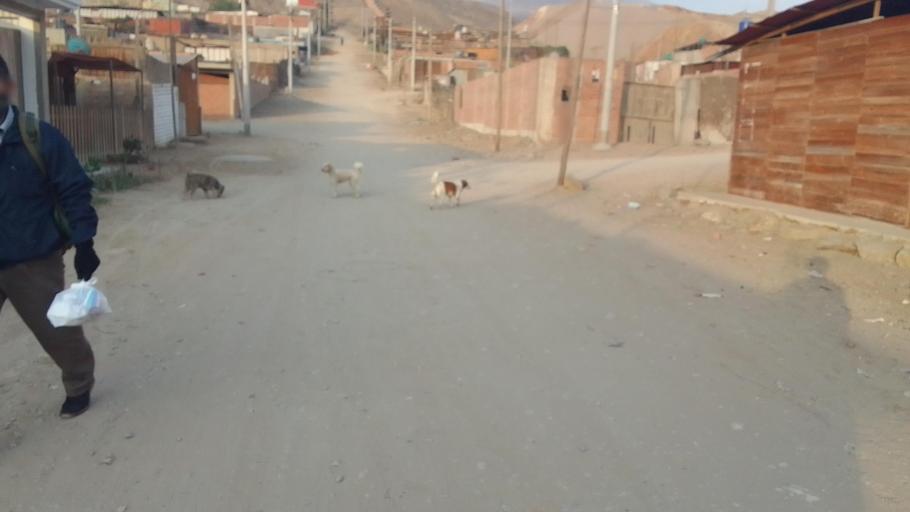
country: PE
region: Lima
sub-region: Lima
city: Santa Rosa
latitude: -11.8179
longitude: -77.1219
